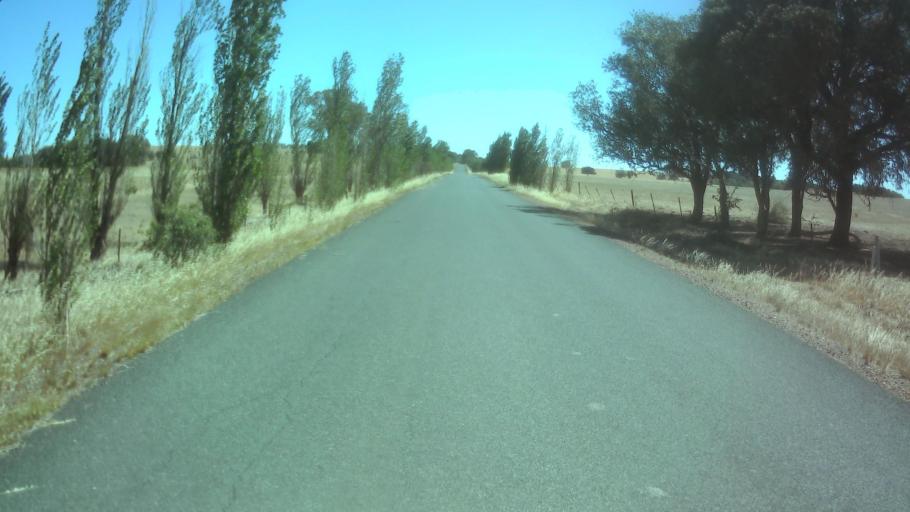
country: AU
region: New South Wales
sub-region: Weddin
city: Grenfell
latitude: -33.9742
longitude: 148.4041
